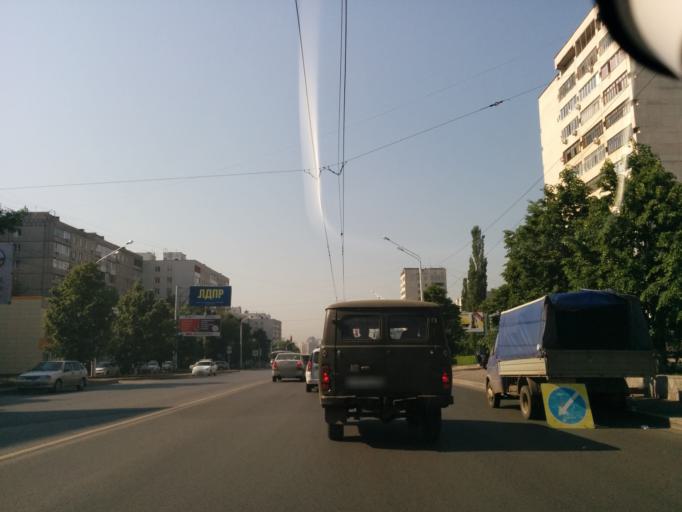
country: RU
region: Bashkortostan
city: Ufa
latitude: 54.7303
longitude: 55.9782
